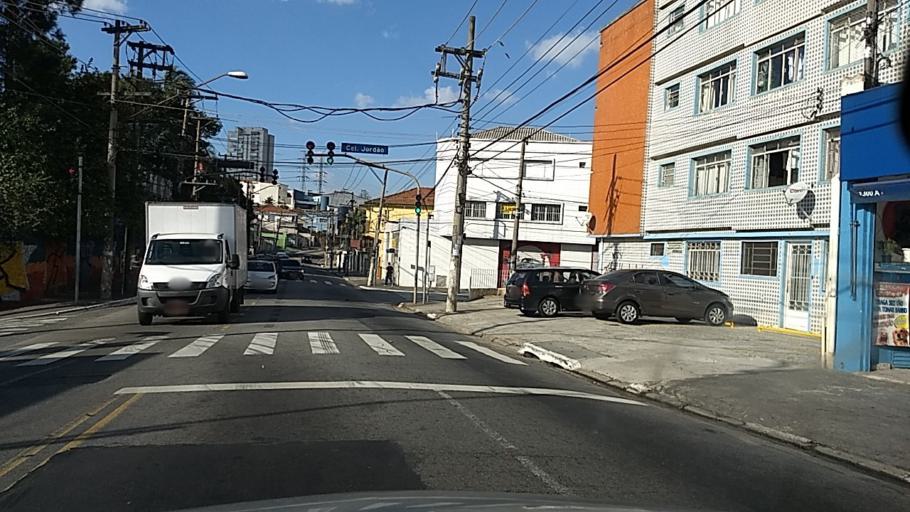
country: BR
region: Sao Paulo
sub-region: Sao Paulo
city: Sao Paulo
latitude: -23.5007
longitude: -46.6010
